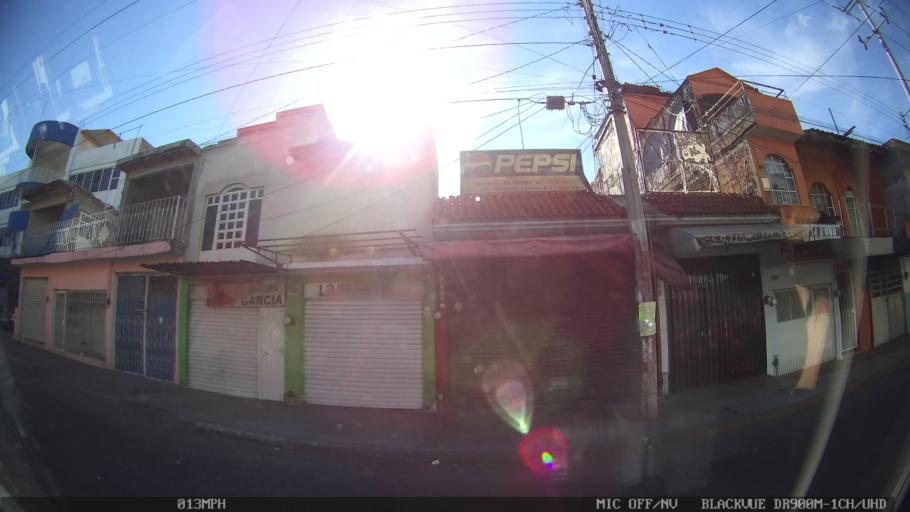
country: MX
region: Jalisco
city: Tlaquepaque
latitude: 20.6932
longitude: -103.2729
